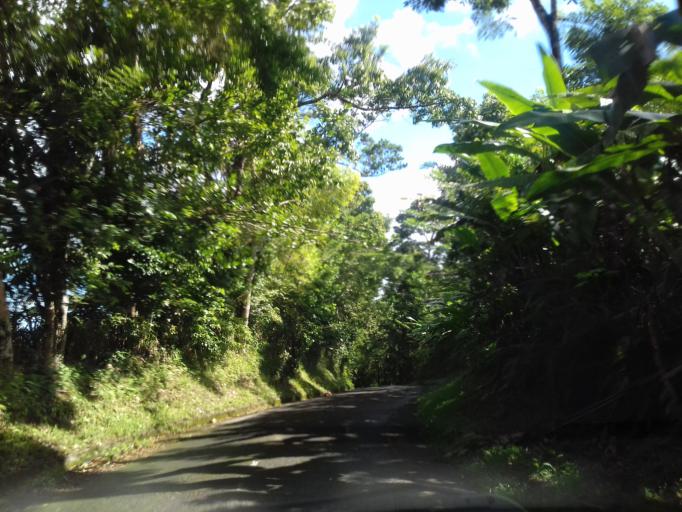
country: MQ
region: Martinique
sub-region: Martinique
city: Saint-Joseph
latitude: 14.6966
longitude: -61.0373
